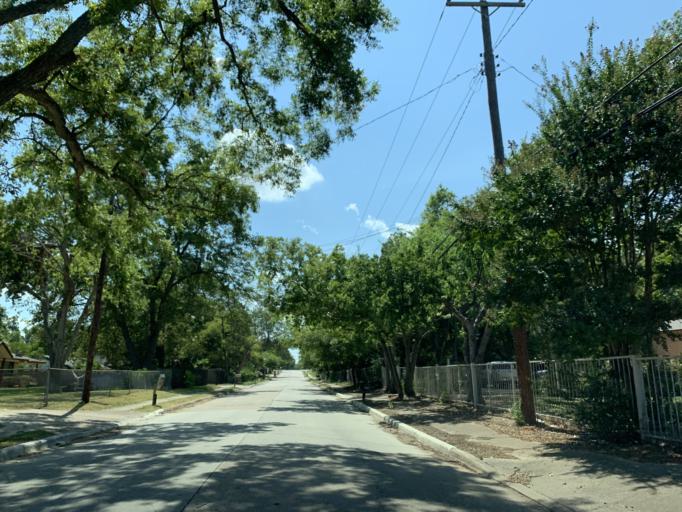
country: US
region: Texas
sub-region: Dallas County
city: Hutchins
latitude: 32.7105
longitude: -96.7663
